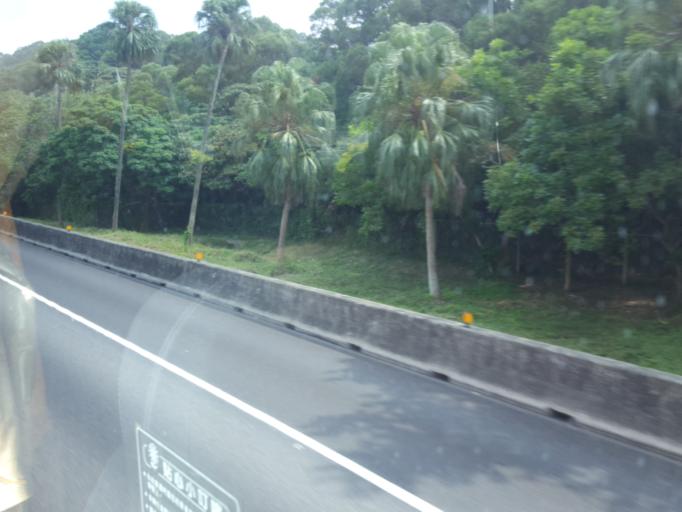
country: TW
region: Taiwan
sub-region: Hsinchu
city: Zhubei
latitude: 24.8847
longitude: 121.0830
